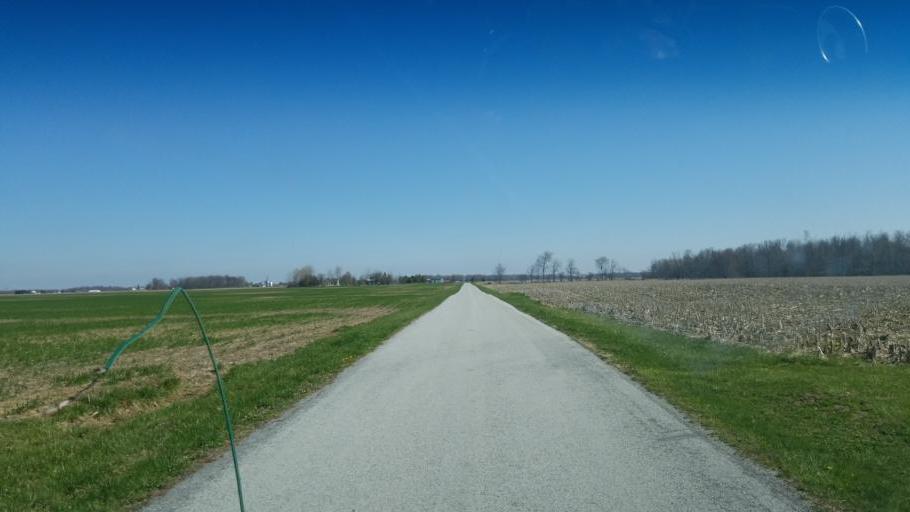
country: US
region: Ohio
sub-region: Hardin County
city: Kenton
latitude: 40.6879
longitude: -83.5593
